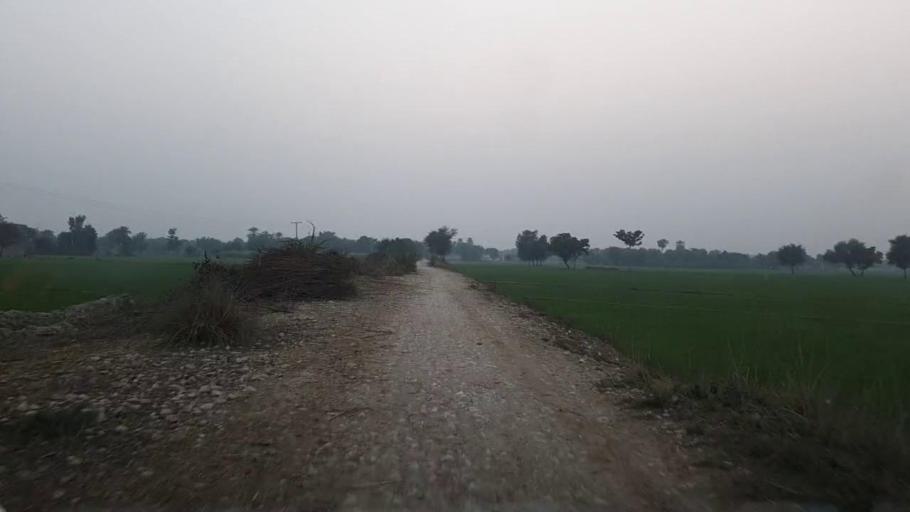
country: PK
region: Sindh
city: Kandiari
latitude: 26.9590
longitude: 68.4604
